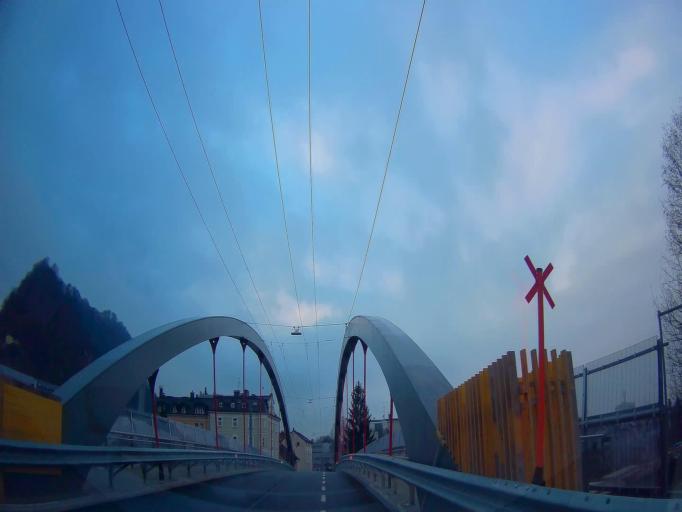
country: AT
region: Salzburg
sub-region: Salzburg Stadt
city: Salzburg
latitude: 47.8090
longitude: 13.0680
